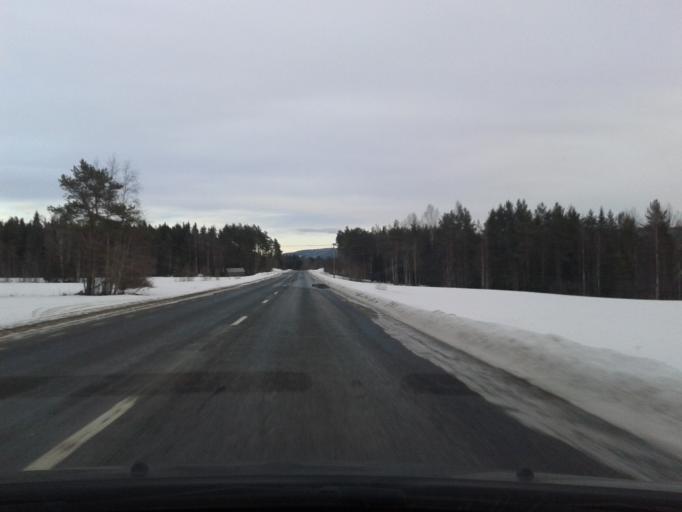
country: SE
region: Vaesternorrland
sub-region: Solleftea Kommun
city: Solleftea
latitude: 63.3406
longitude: 17.0751
